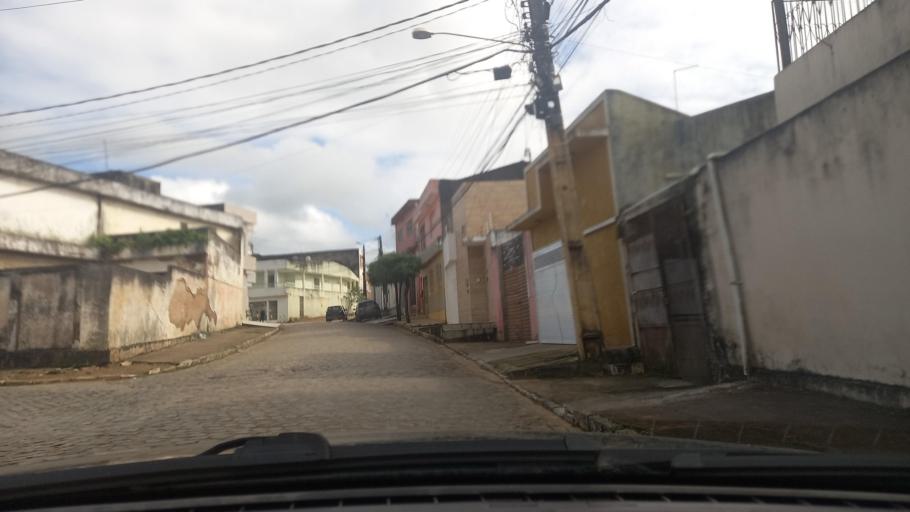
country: BR
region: Pernambuco
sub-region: Vitoria De Santo Antao
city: Vitoria de Santo Antao
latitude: -8.1083
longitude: -35.2980
